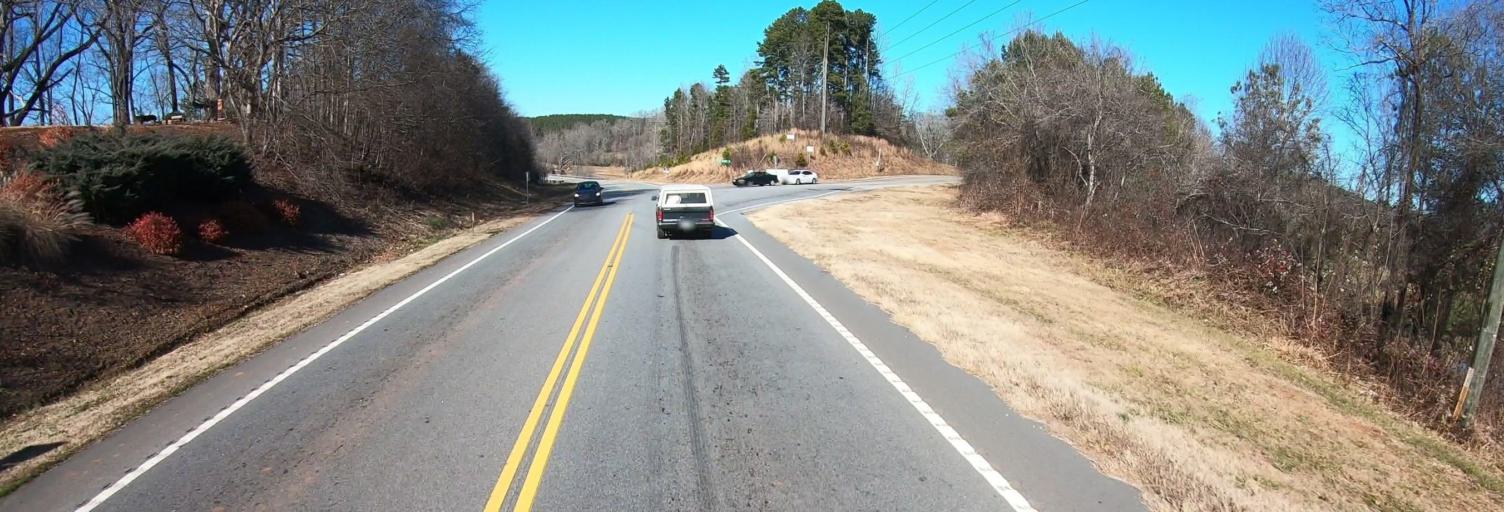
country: US
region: South Carolina
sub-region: Oconee County
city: Walhalla
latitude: 34.7844
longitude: -83.0283
